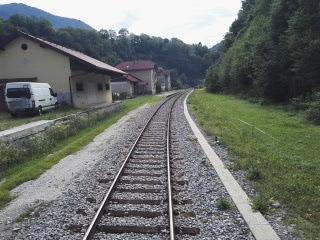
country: SI
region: Tolmin
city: Tolmin
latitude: 46.1595
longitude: 13.8132
